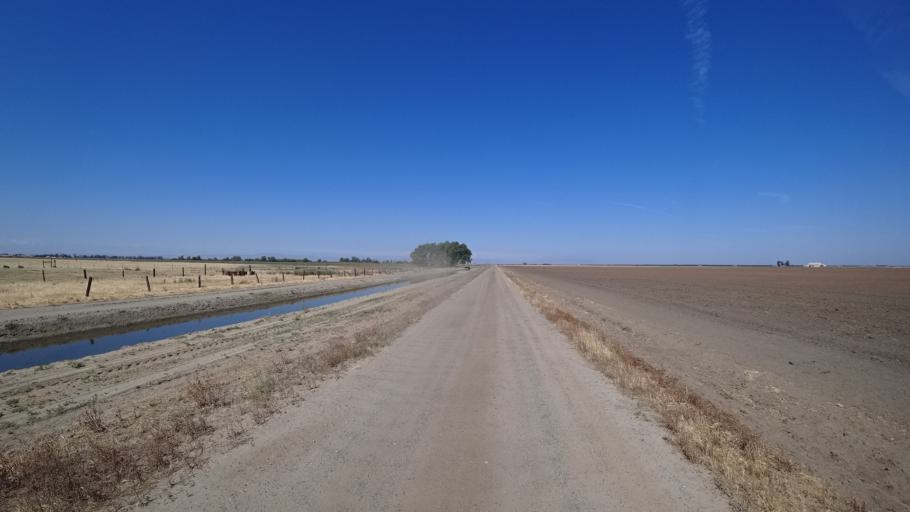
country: US
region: California
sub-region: Kings County
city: Stratford
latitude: 36.2115
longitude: -119.8184
